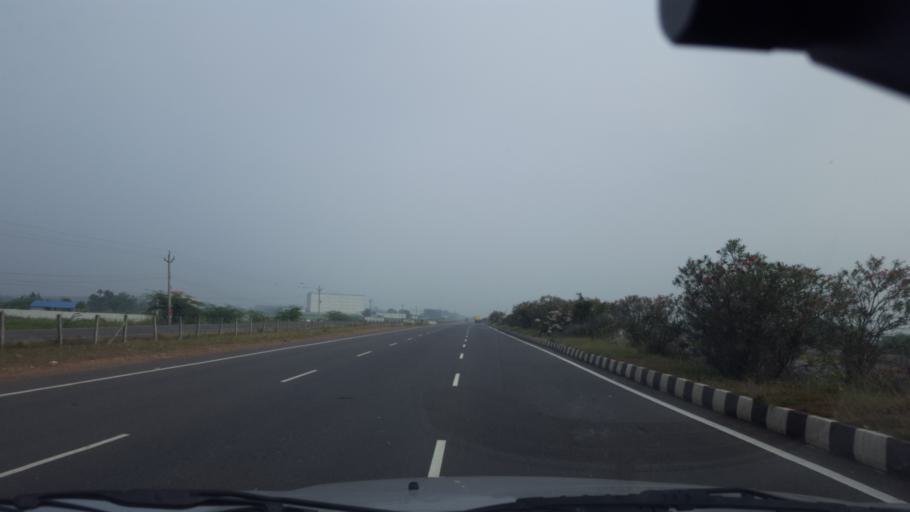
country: IN
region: Andhra Pradesh
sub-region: Guntur
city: Chilakalurupet
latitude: 16.0344
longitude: 80.1321
